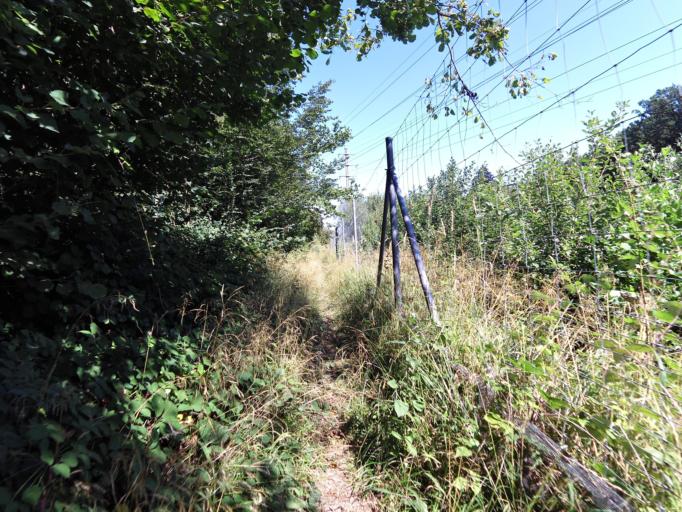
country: CH
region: Thurgau
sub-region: Kreuzlingen District
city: Tagerwilen
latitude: 47.6308
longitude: 9.1431
